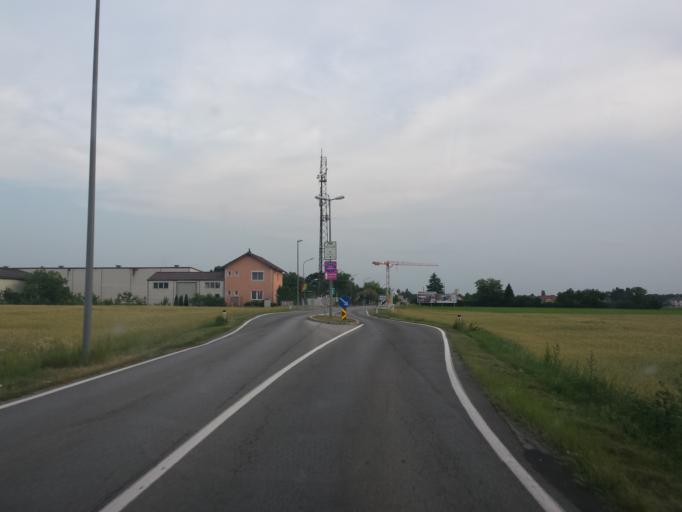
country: AT
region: Lower Austria
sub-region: Politischer Bezirk Ganserndorf
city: Deutsch-Wagram
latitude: 48.3227
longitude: 16.5827
